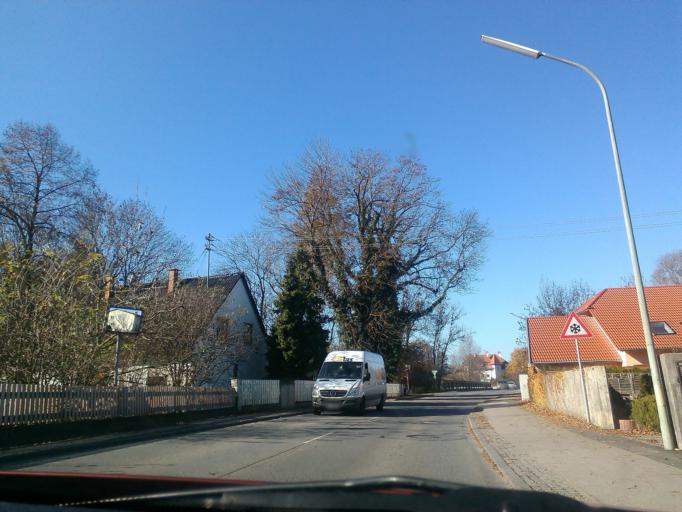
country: DE
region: Bavaria
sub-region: Upper Bavaria
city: Olching
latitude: 48.2243
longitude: 11.3453
